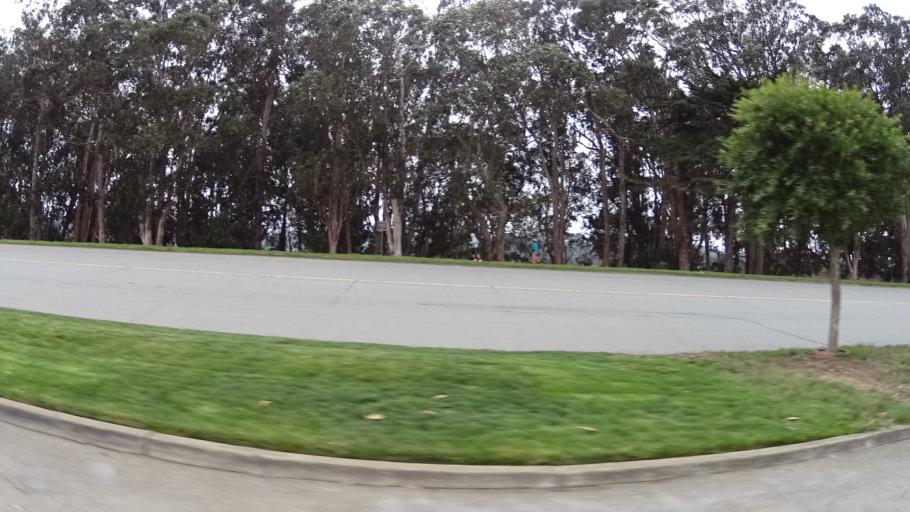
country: US
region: California
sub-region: San Mateo County
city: Daly City
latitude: 37.7291
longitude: -122.4963
